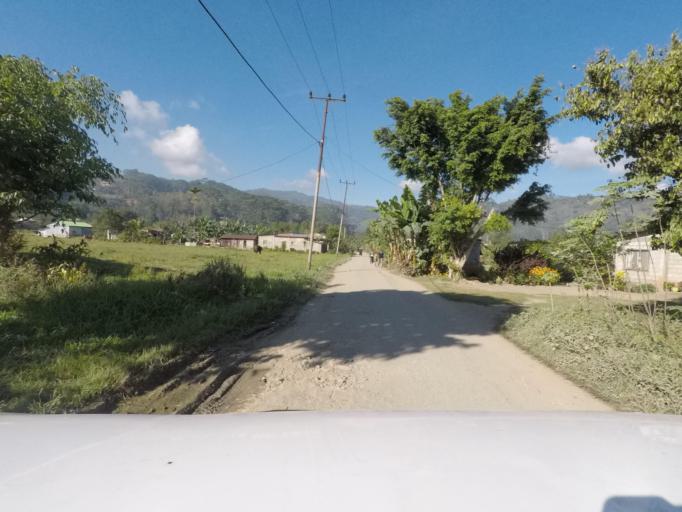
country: TL
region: Ermera
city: Gleno
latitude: -8.7263
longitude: 125.4339
